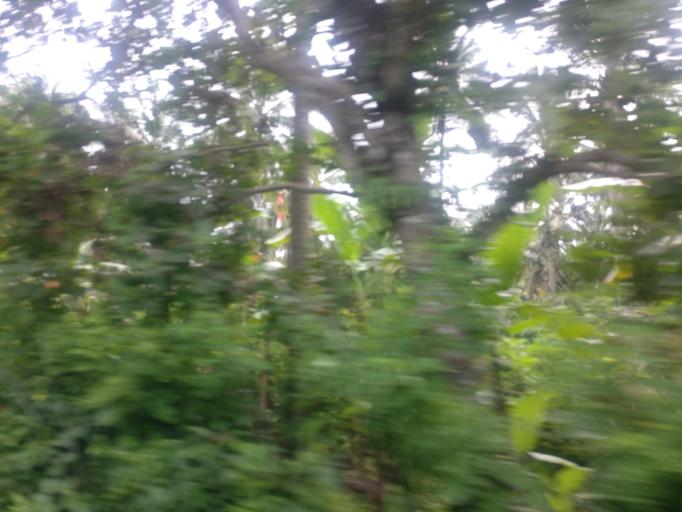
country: ID
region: Bali
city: Banjar Kawan
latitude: -8.4911
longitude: 115.5160
